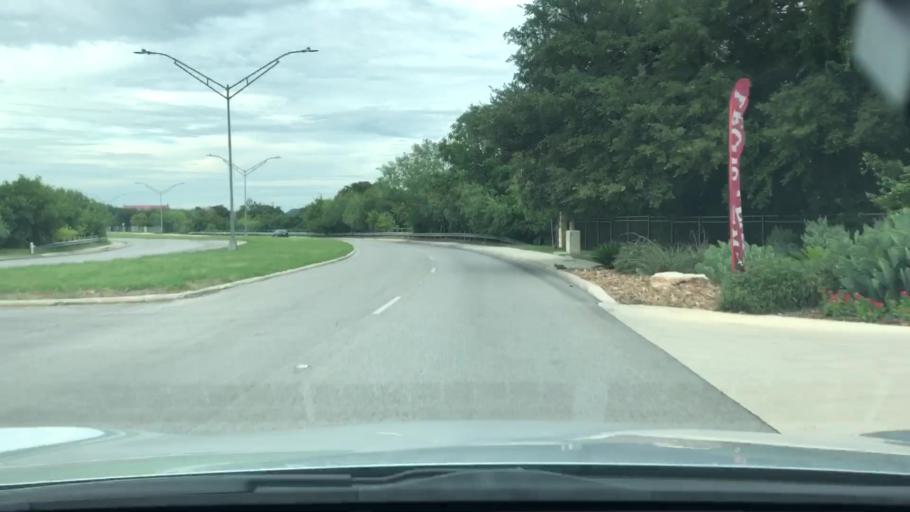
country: US
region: Texas
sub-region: Bexar County
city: Leon Valley
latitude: 29.4482
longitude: -98.6697
